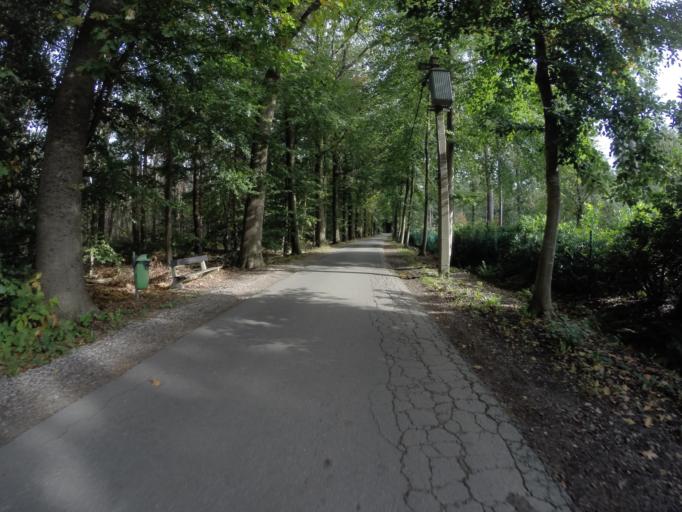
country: BE
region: Flanders
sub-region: Provincie West-Vlaanderen
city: Ruiselede
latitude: 51.0842
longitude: 3.3748
